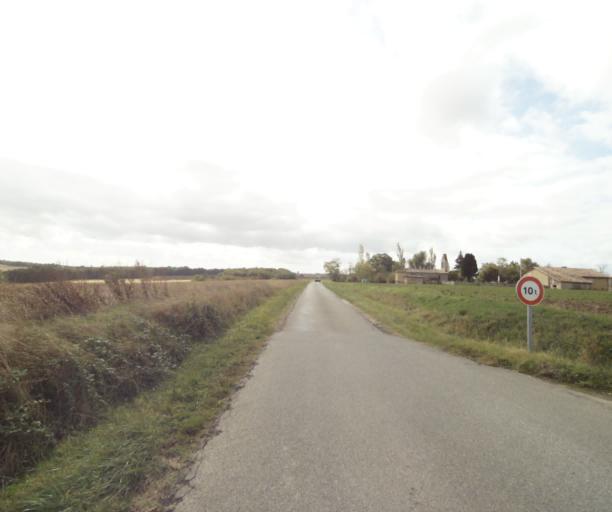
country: FR
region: Midi-Pyrenees
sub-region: Departement du Tarn-et-Garonne
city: Beaumont-de-Lomagne
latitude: 43.8782
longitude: 1.0831
